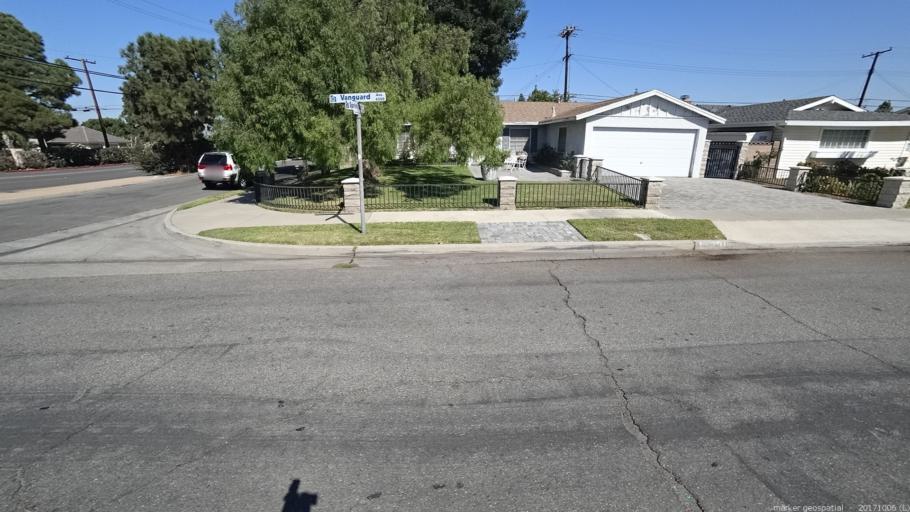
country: US
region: California
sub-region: Orange County
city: Stanton
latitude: 33.7875
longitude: -118.0195
